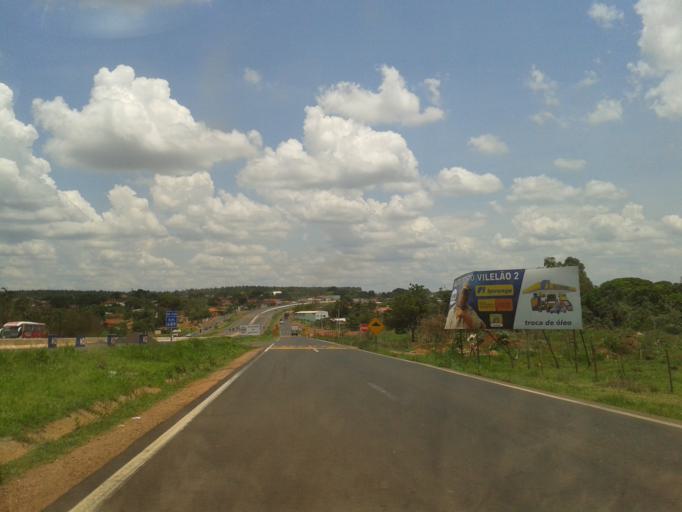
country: BR
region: Minas Gerais
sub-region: Monte Alegre De Minas
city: Monte Alegre de Minas
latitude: -18.8705
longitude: -48.8707
